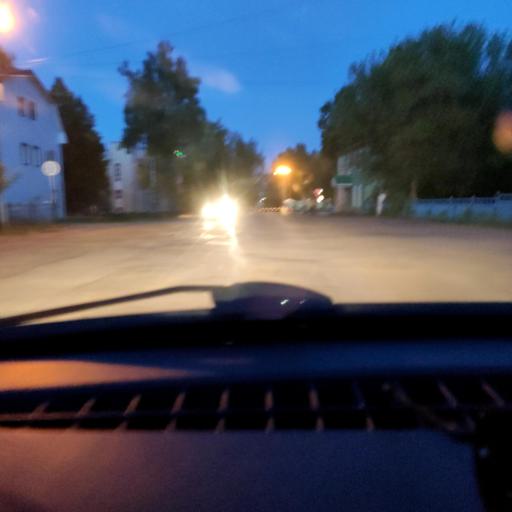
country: RU
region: Bashkortostan
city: Karmaskaly
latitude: 54.3697
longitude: 56.1688
